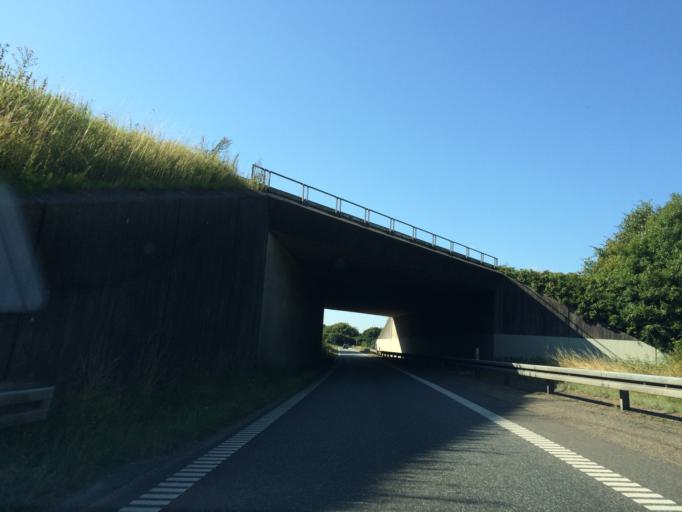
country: DK
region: South Denmark
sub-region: Kolding Kommune
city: Kolding
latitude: 55.5339
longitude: 9.4980
